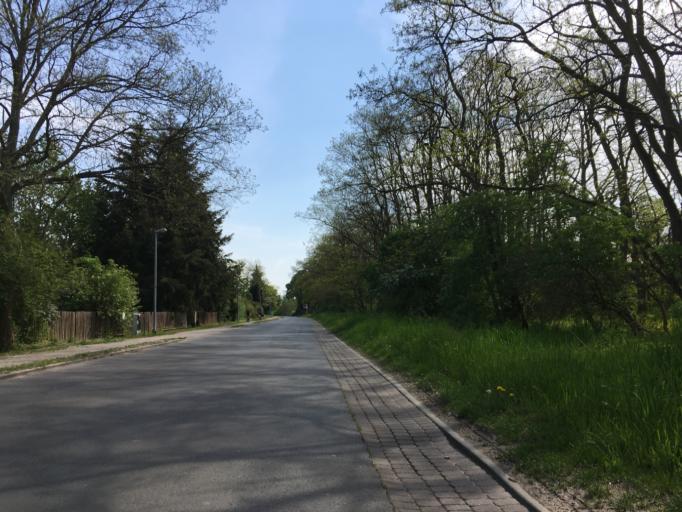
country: DE
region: Brandenburg
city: Werneuchen
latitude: 52.6006
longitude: 13.7506
